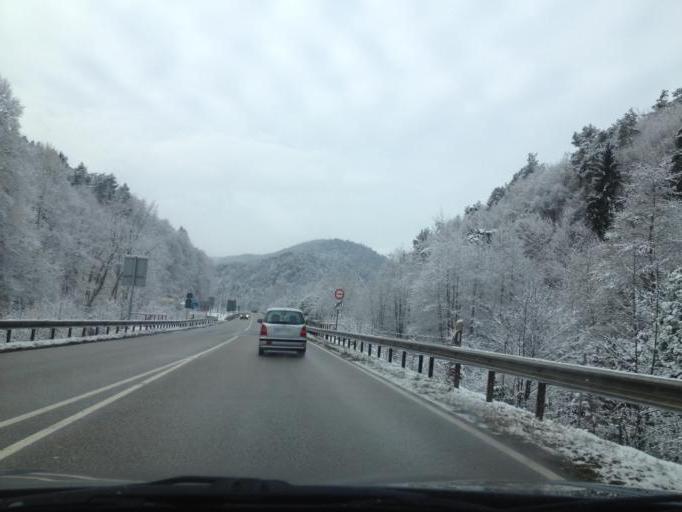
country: DE
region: Rheinland-Pfalz
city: Rinnthal
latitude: 49.2246
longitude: 7.9113
